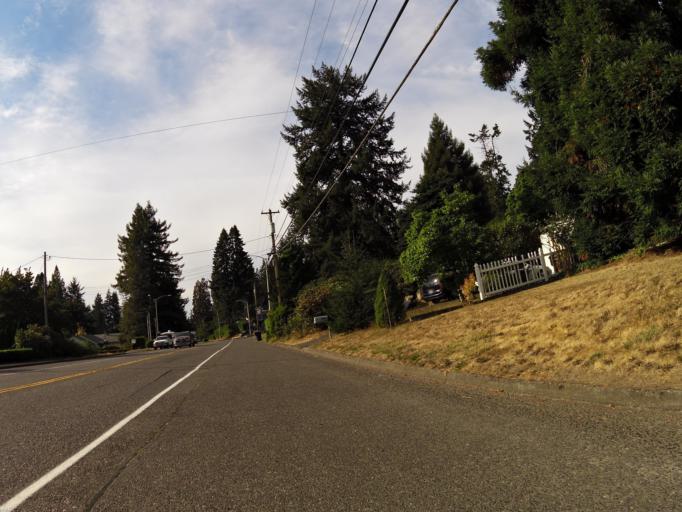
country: US
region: Washington
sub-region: Cowlitz County
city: Longview Heights
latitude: 46.1638
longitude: -122.9627
